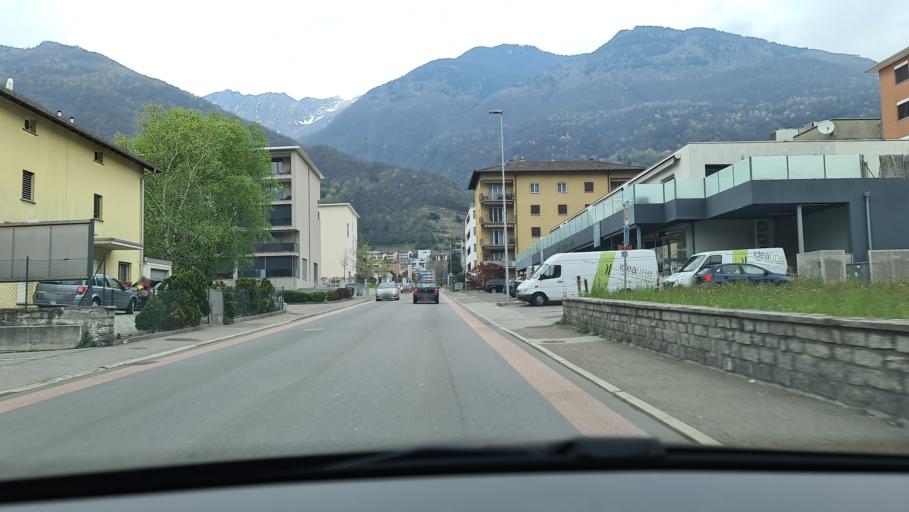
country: CH
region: Ticino
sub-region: Bellinzona District
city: Sementina
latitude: 46.1805
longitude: 8.9938
